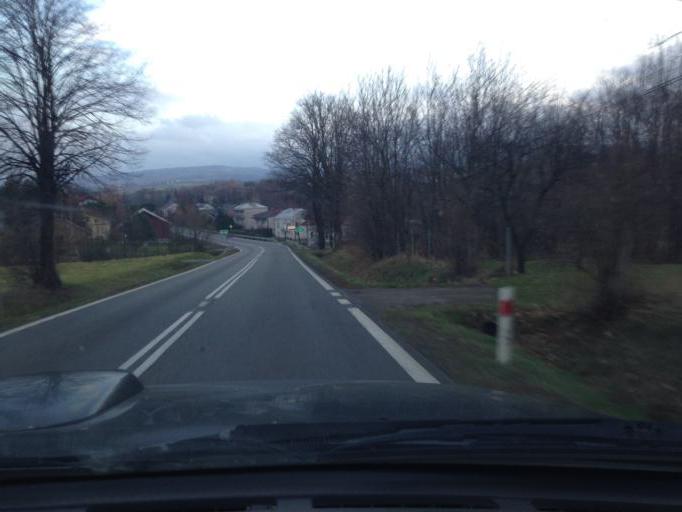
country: PL
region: Subcarpathian Voivodeship
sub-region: Powiat jasielski
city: Nowy Zmigrod
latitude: 49.6252
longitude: 21.5352
